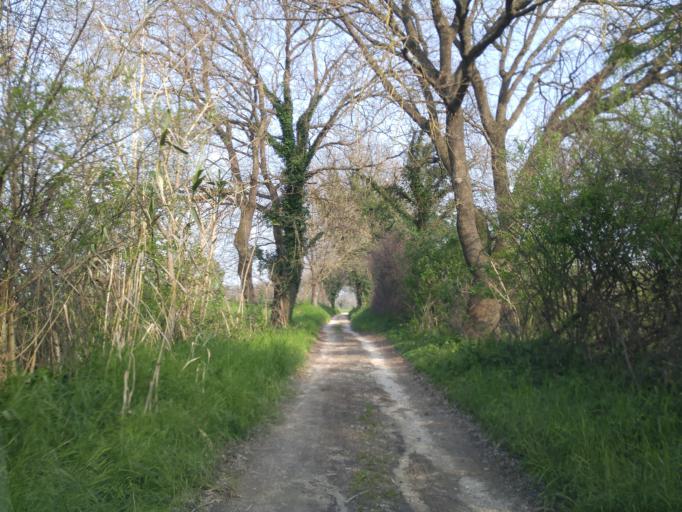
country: IT
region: The Marches
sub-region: Provincia di Pesaro e Urbino
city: Sant'Ippolito
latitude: 43.7036
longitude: 12.8513
